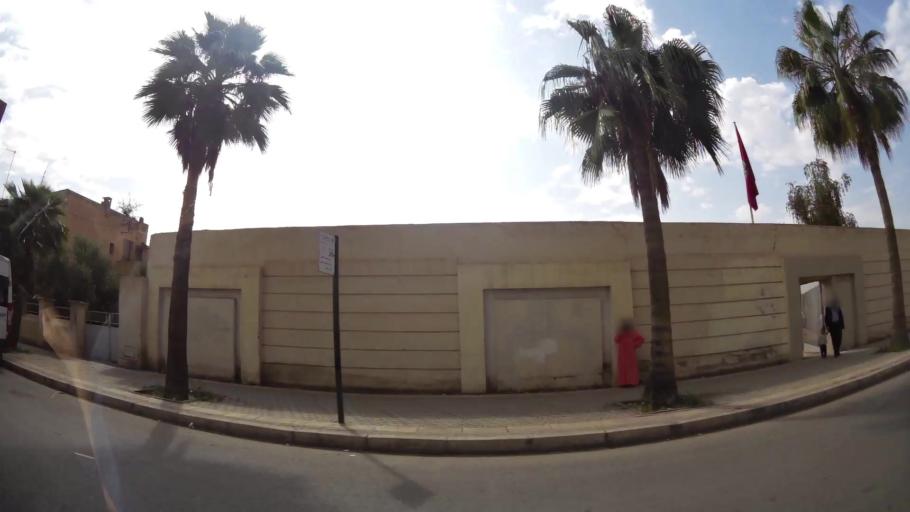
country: MA
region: Oriental
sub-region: Oujda-Angad
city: Oujda
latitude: 34.6872
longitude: -1.9118
